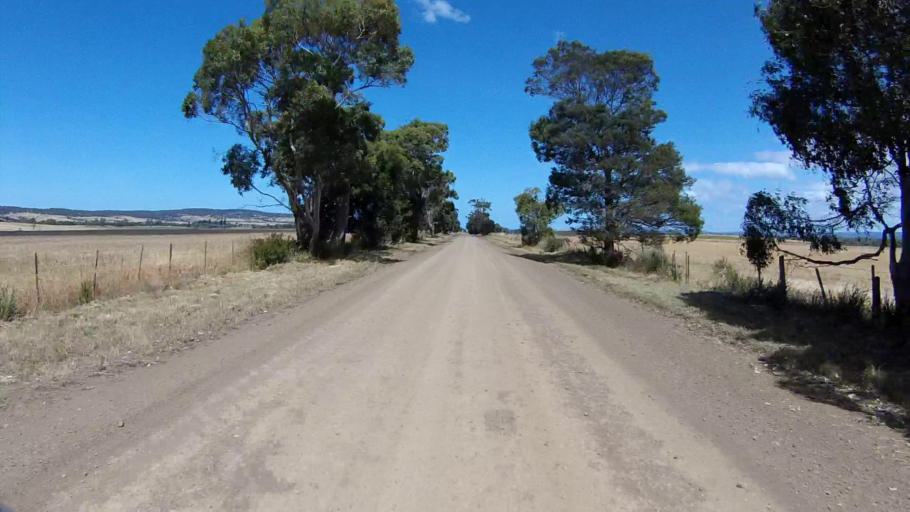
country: AU
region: Tasmania
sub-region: Break O'Day
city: St Helens
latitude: -41.9876
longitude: 148.0664
